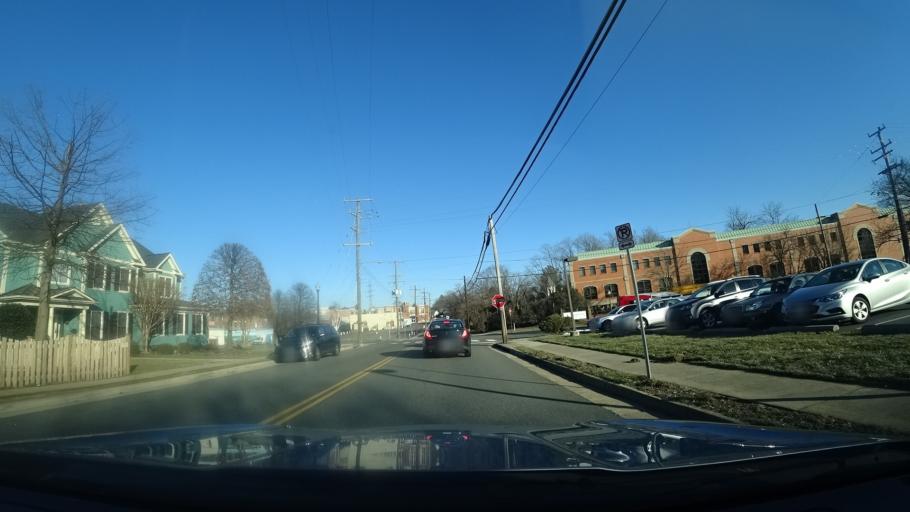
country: US
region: Virginia
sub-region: Fairfax County
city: Herndon
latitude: 38.9687
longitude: -77.3885
